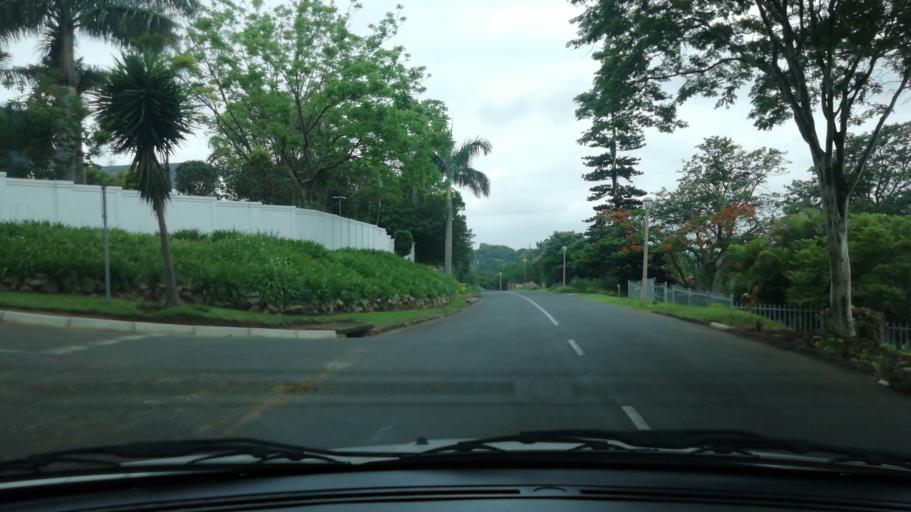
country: ZA
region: KwaZulu-Natal
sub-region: uThungulu District Municipality
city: Empangeni
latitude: -28.7599
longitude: 31.8885
